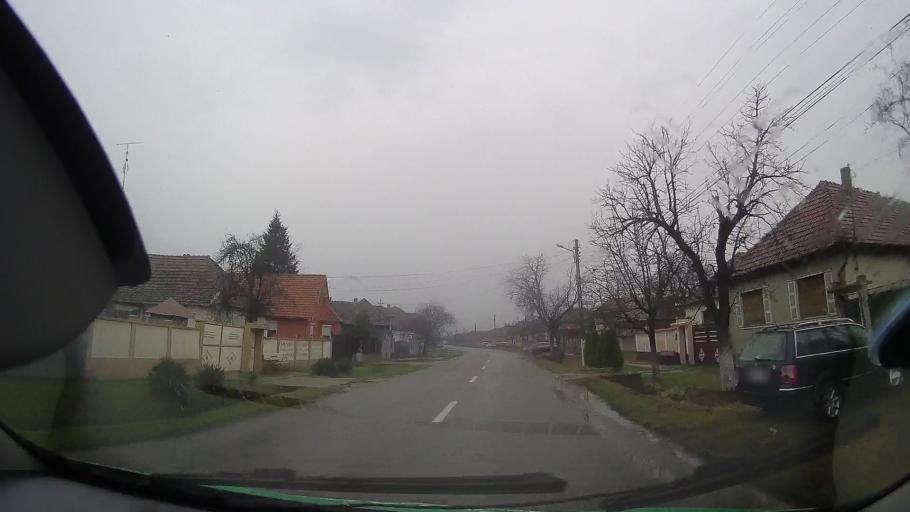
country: RO
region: Bihor
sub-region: Comuna Tulca
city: Tulca
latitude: 46.7916
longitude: 21.7705
